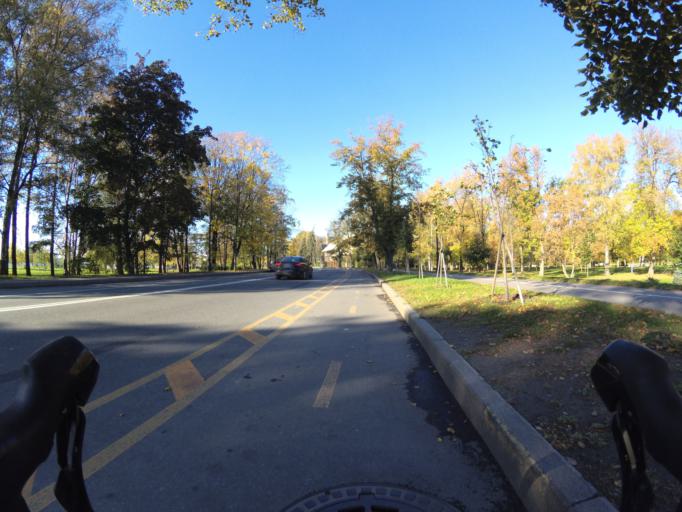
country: RU
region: Leningrad
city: Krestovskiy ostrov
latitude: 59.9682
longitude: 30.2405
